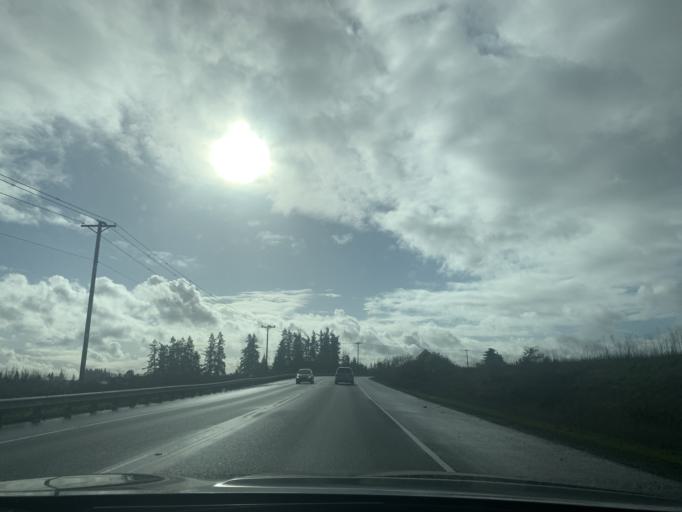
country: US
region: Oregon
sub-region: Washington County
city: Sherwood
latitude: 45.3854
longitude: -122.8521
